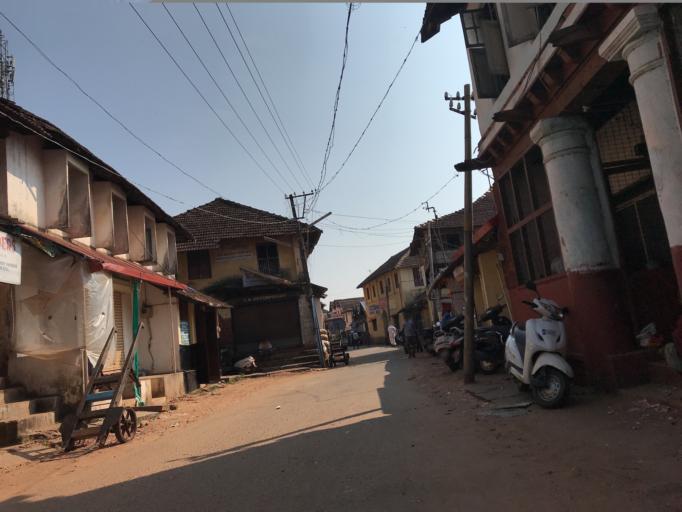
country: IN
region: Karnataka
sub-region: Dakshina Kannada
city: Mangalore
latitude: 12.8634
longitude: 74.8330
